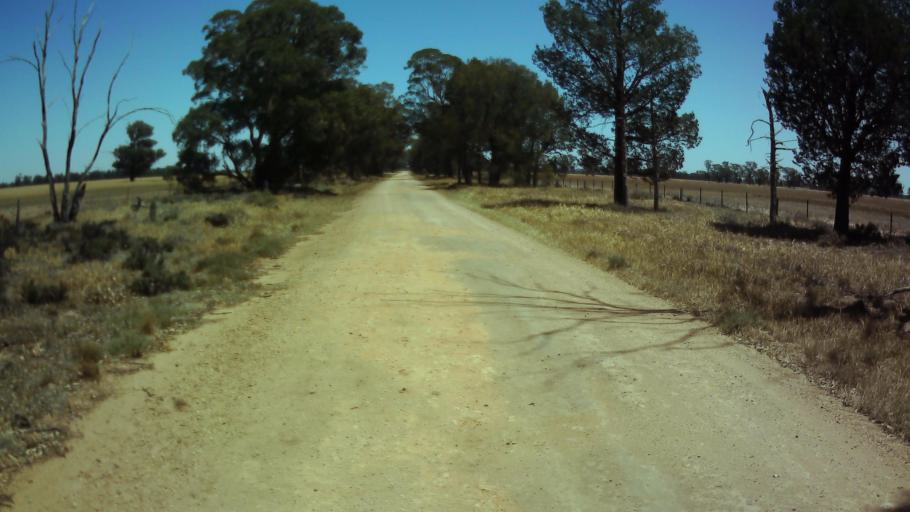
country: AU
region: New South Wales
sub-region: Weddin
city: Grenfell
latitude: -34.0083
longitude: 147.9637
